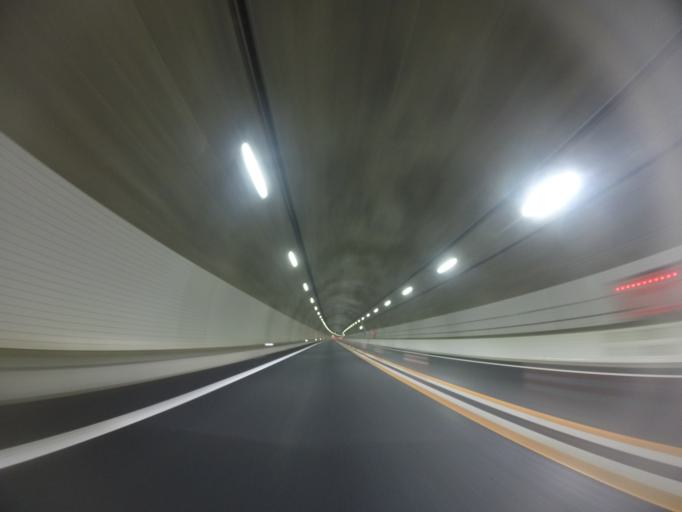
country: JP
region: Shizuoka
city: Shizuoka-shi
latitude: 35.1326
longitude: 138.4507
